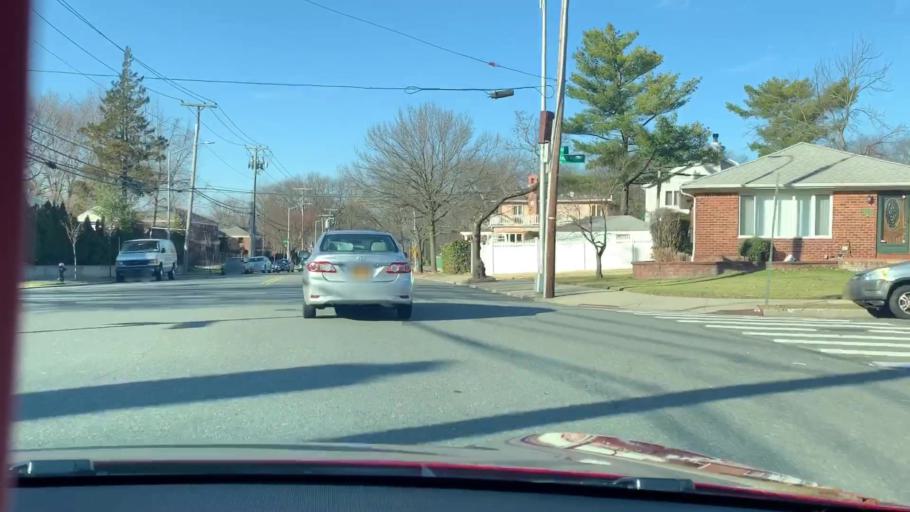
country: US
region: New York
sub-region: Nassau County
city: Bellerose Terrace
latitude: 40.7384
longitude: -73.7487
